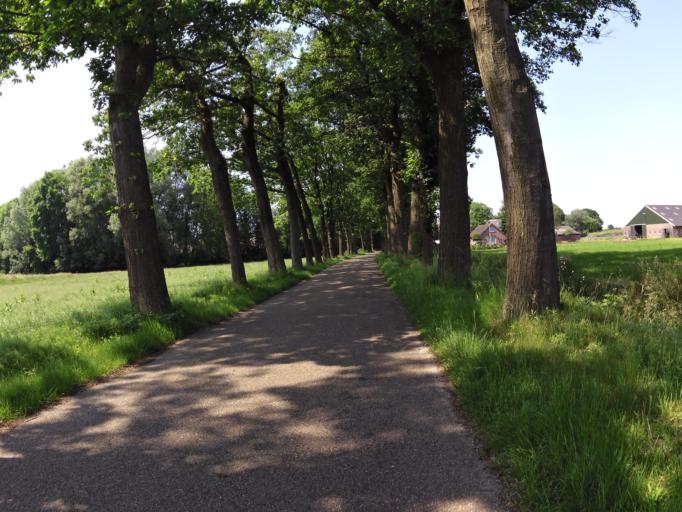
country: NL
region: North Brabant
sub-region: Gemeente Sint-Michielsgestel
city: Sint-Michielsgestel
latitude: 51.6279
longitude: 5.3575
